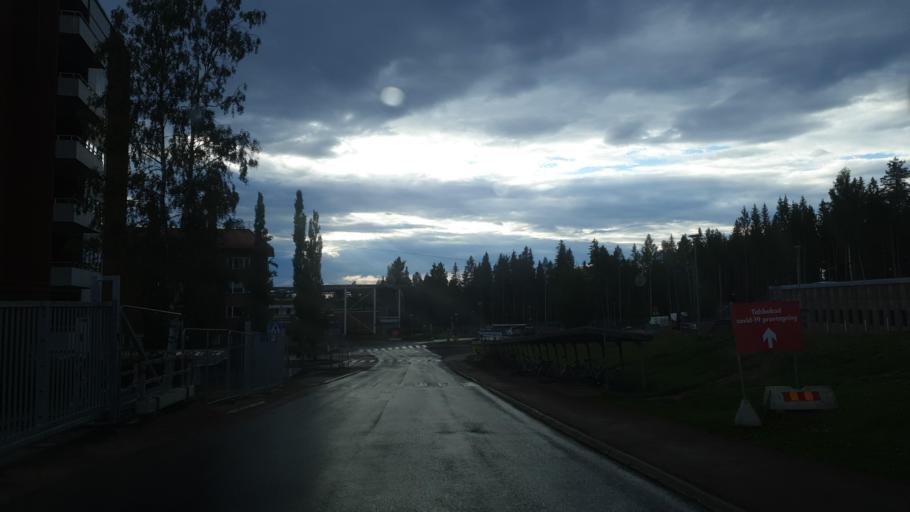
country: SE
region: Dalarna
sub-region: Mora Kommun
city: Mora
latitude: 61.0164
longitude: 14.5865
